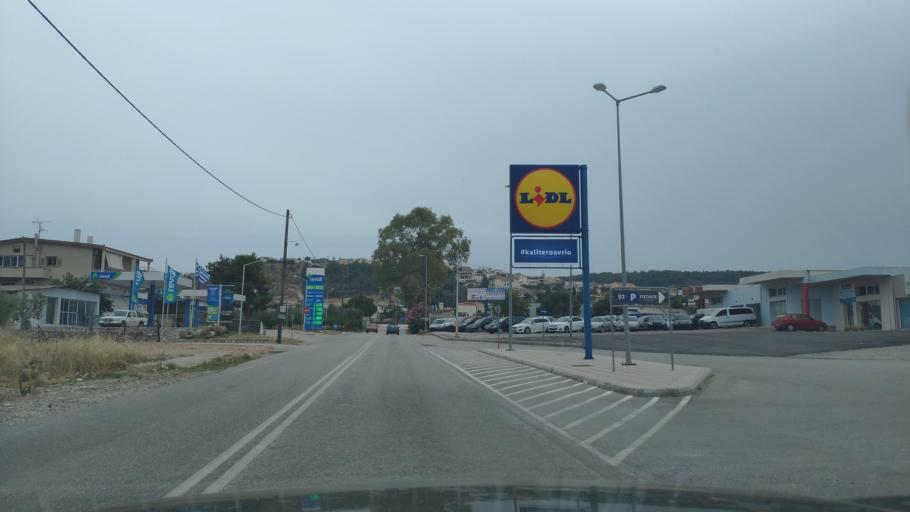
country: GR
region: Peloponnese
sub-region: Nomos Argolidos
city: Kranidi
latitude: 37.3901
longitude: 23.1578
